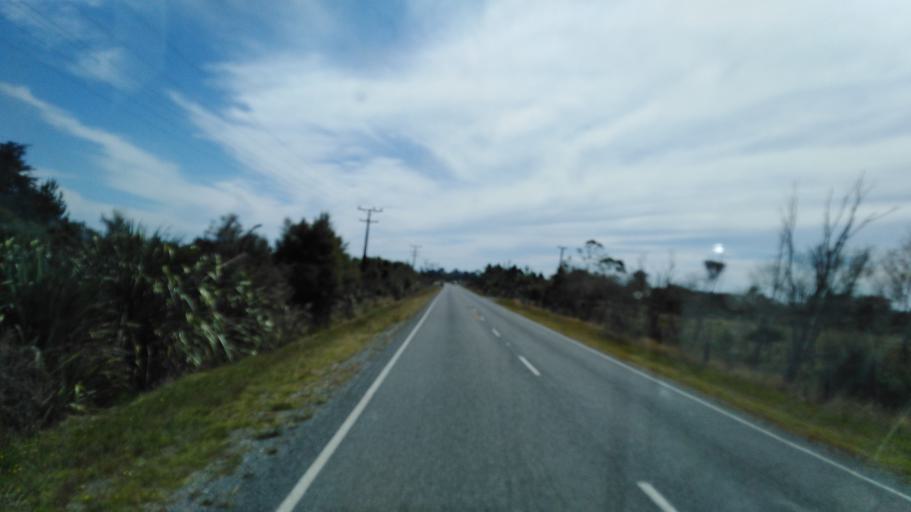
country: NZ
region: West Coast
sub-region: Buller District
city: Westport
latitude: -41.7394
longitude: 171.7085
